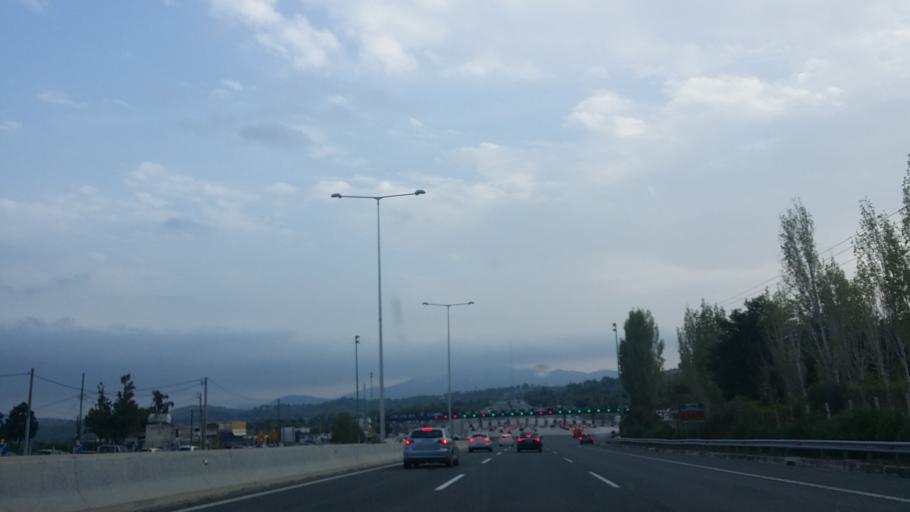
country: GR
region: Attica
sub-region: Nomarchia Anatolikis Attikis
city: Afidnes
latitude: 38.1804
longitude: 23.8532
